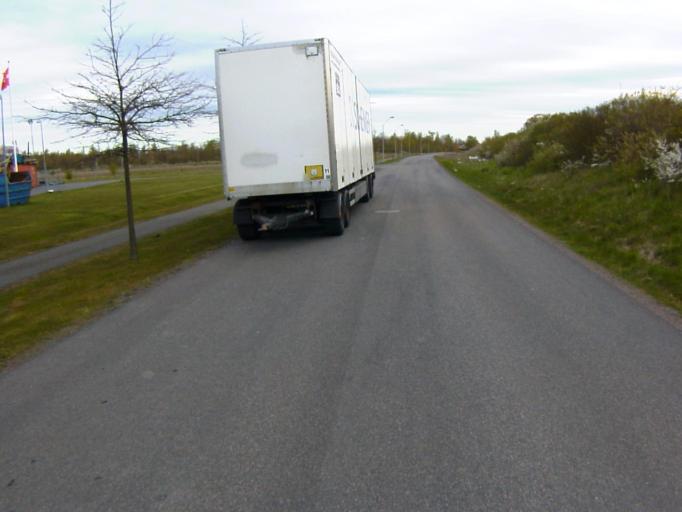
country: SE
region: Skane
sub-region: Kristianstads Kommun
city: Kristianstad
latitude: 56.0233
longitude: 14.1202
